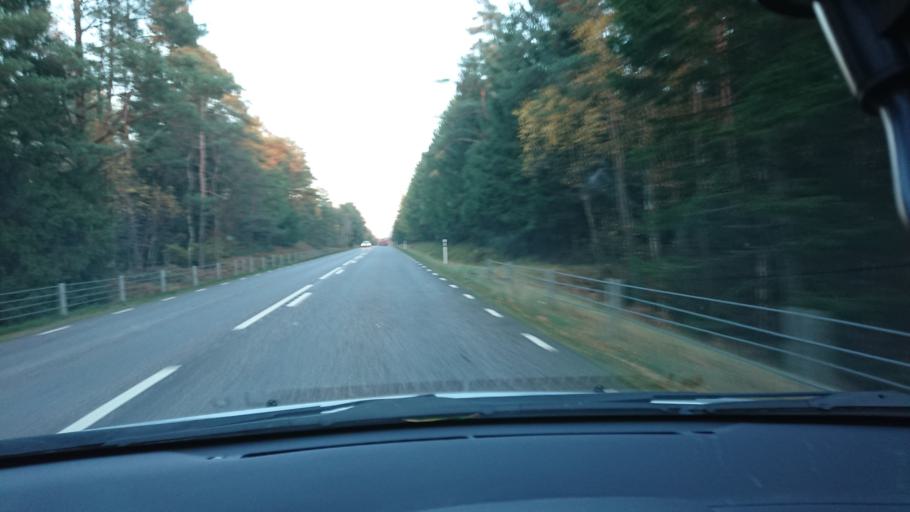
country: SE
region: Halland
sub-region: Laholms Kommun
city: Knared
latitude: 56.7146
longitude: 13.2078
